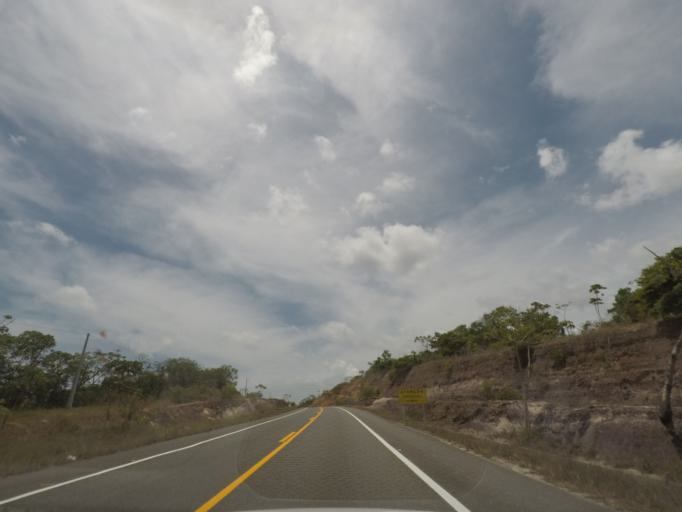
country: BR
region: Bahia
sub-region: Conde
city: Conde
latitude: -11.7001
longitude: -37.5722
